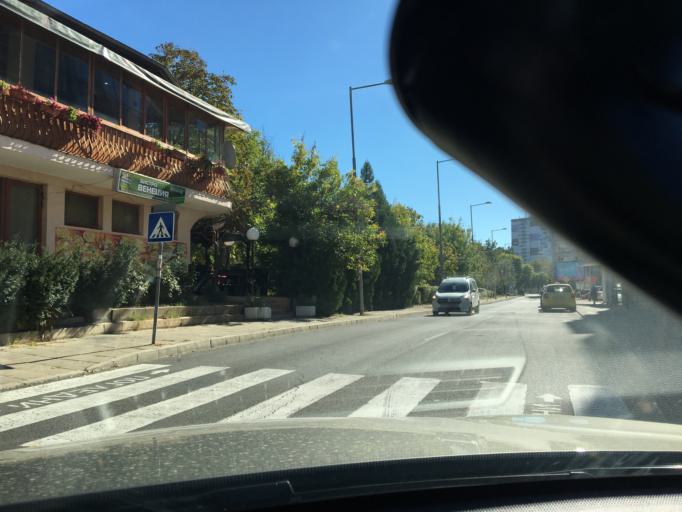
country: BG
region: Burgas
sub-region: Obshtina Burgas
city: Burgas
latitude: 42.5185
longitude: 27.4526
